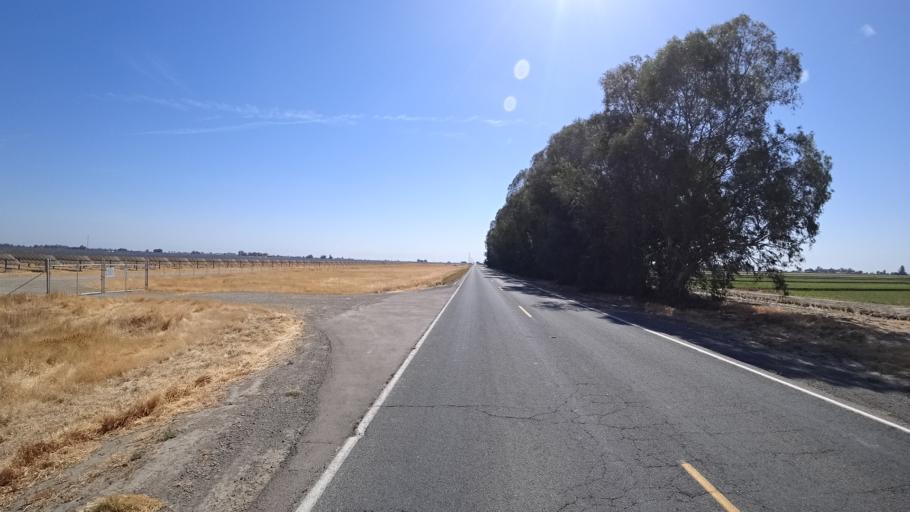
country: US
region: California
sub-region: Kings County
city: Stratford
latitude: 36.2115
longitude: -119.8071
